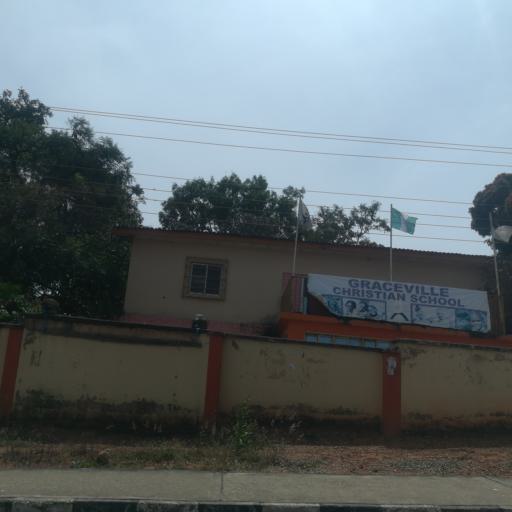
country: NG
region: Plateau
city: Jos
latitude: 9.9093
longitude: 8.8804
